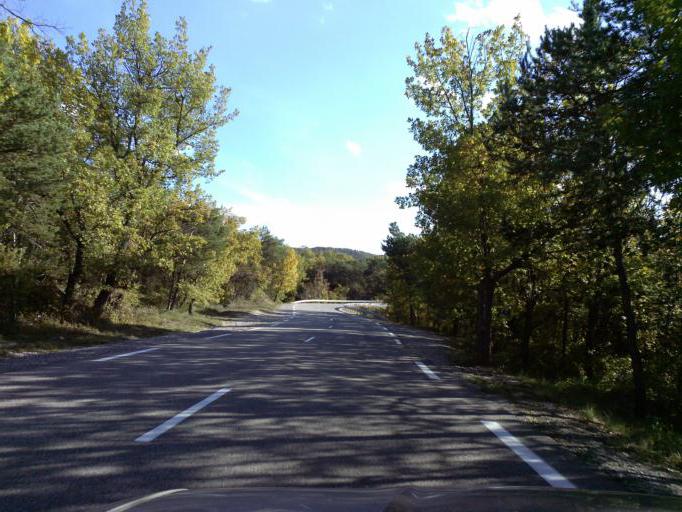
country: FR
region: Provence-Alpes-Cote d'Azur
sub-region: Departement des Alpes-de-Haute-Provence
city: Riez
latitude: 43.9134
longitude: 6.1381
